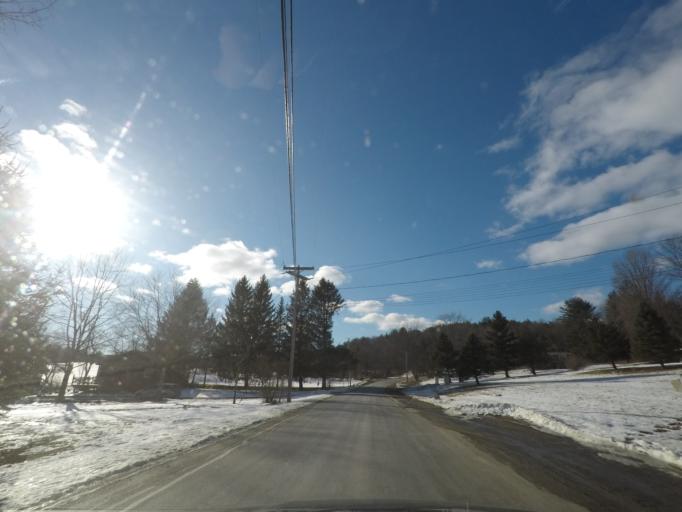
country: US
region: New York
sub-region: Rensselaer County
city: Nassau
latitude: 42.5162
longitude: -73.5178
